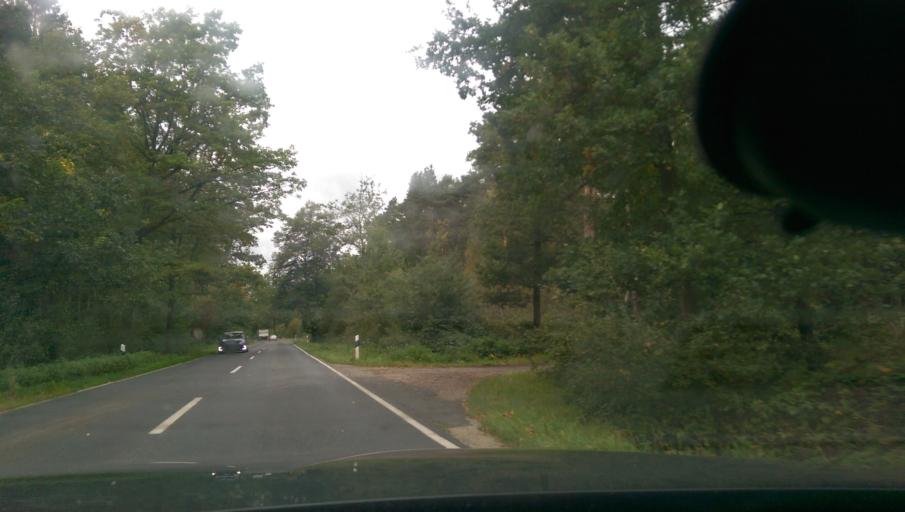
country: DE
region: Lower Saxony
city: Burgdorf
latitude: 52.4770
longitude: 9.9469
